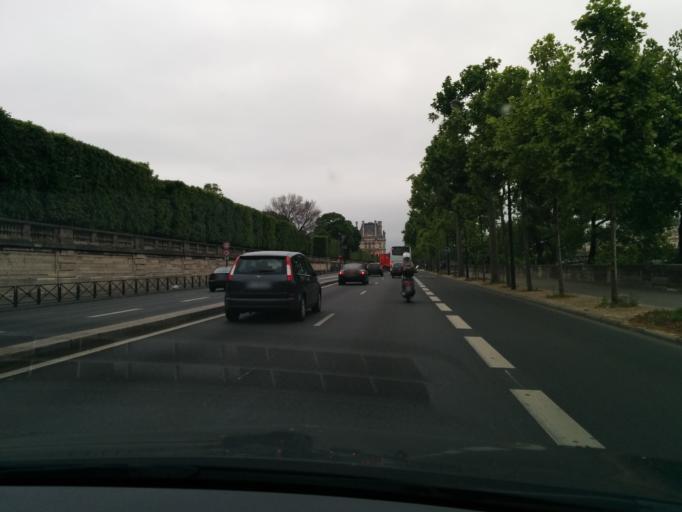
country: FR
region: Ile-de-France
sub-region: Paris
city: Paris
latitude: 48.8632
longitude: 2.3231
